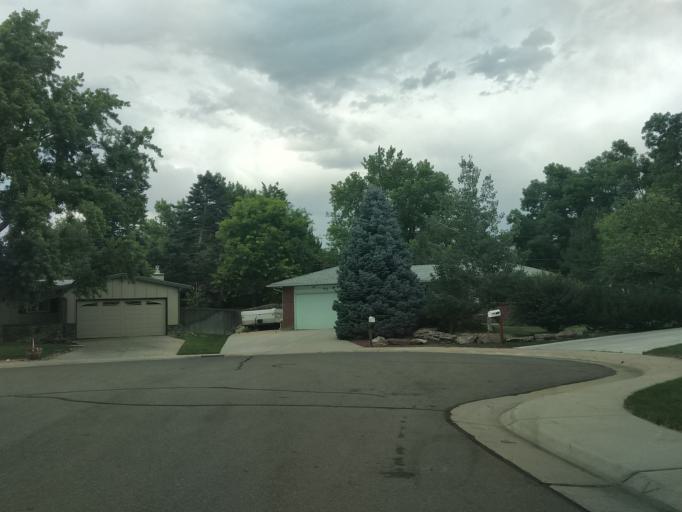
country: US
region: Colorado
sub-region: Jefferson County
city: Lakewood
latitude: 39.6976
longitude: -105.1034
